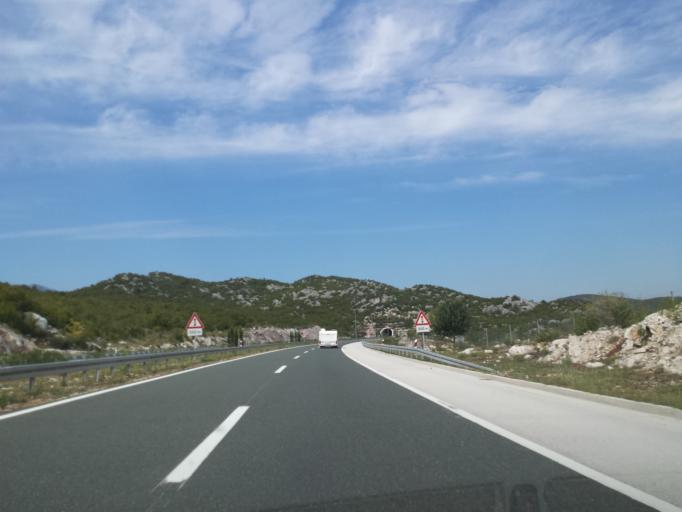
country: HR
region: Splitsko-Dalmatinska
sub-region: Grad Omis
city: Omis
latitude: 43.4804
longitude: 16.8077
